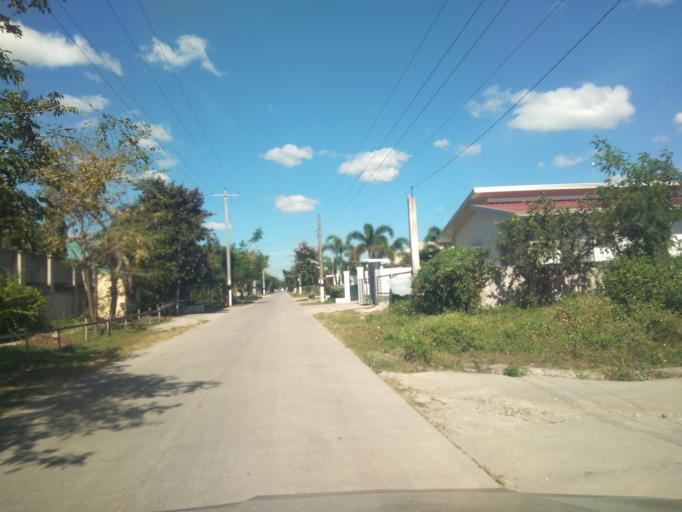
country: PH
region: Central Luzon
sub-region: Province of Pampanga
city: Bacolor
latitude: 15.0132
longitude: 120.6339
